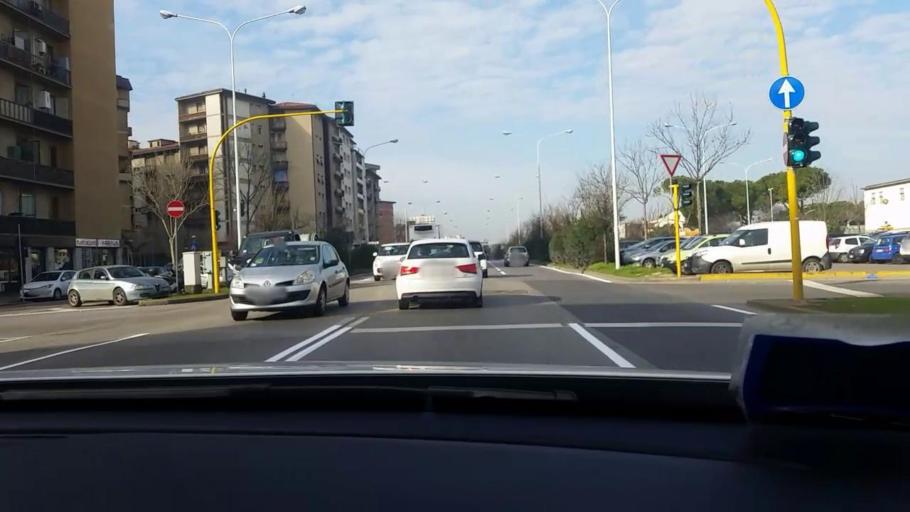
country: IT
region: Tuscany
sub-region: Province of Florence
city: Florence
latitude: 43.7978
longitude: 11.2186
